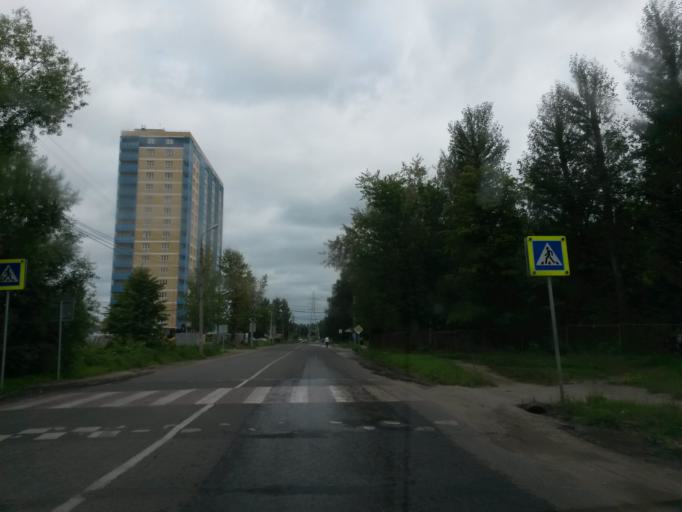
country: RU
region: Jaroslavl
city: Yaroslavl
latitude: 57.5838
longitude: 39.8735
